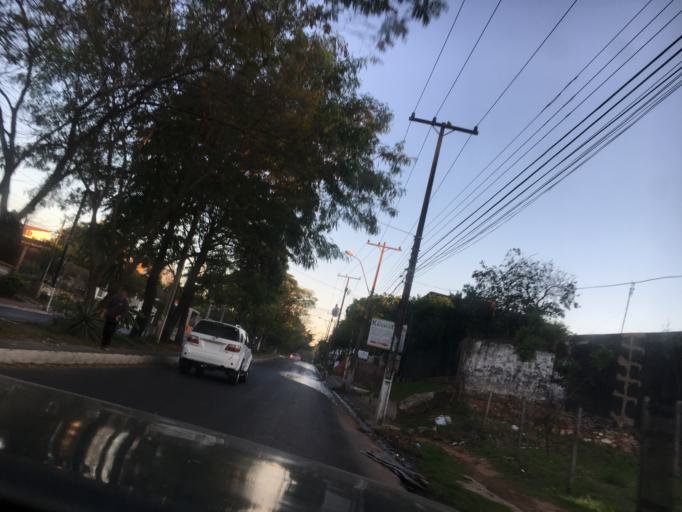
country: PY
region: Central
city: Lambare
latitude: -25.3392
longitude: -57.6055
